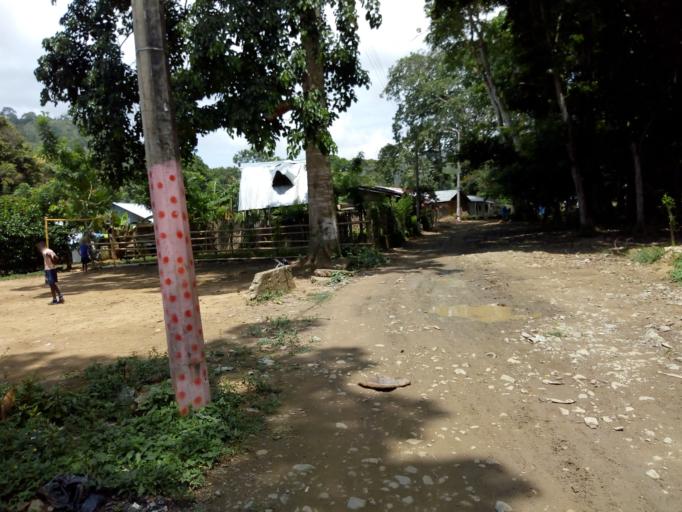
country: PA
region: Guna Yala
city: Puerto Obaldia
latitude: 8.6274
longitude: -77.3554
